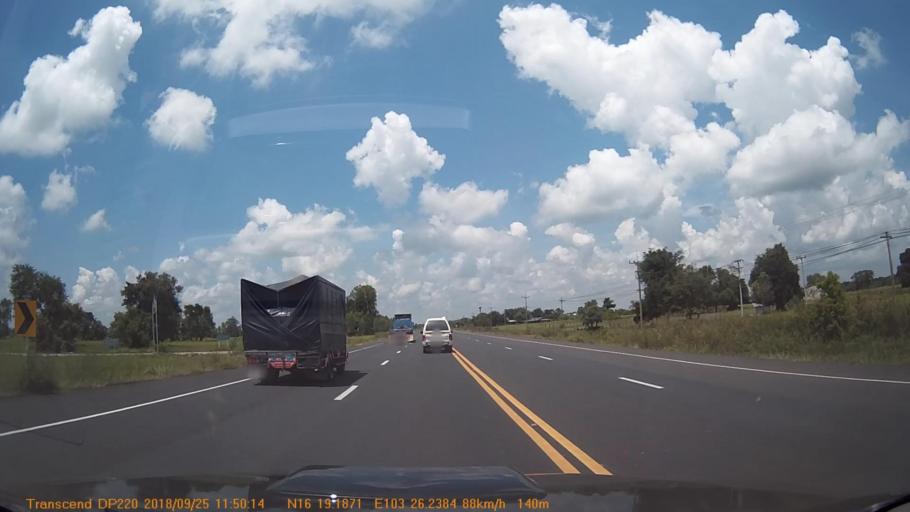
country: TH
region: Kalasin
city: Khong Chai
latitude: 16.3197
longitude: 103.4374
